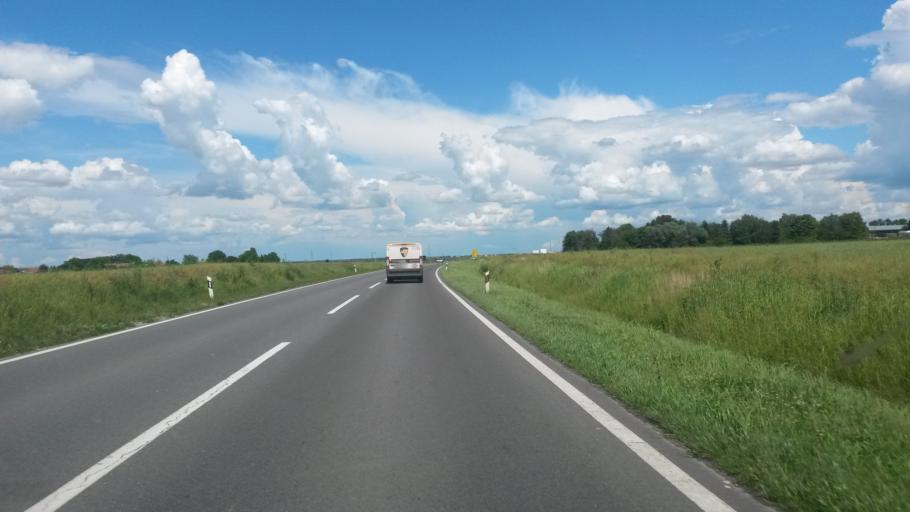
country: HR
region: Osjecko-Baranjska
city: Cepin
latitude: 45.5349
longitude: 18.5545
